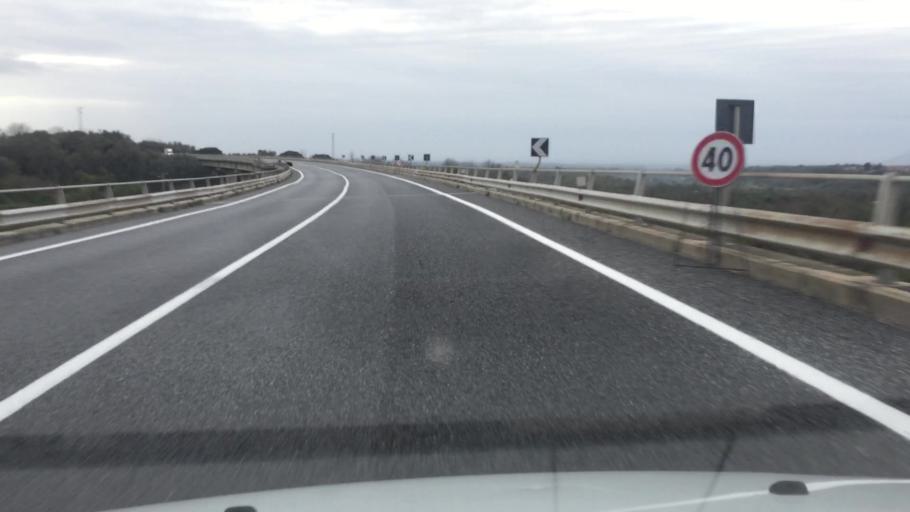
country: IT
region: Calabria
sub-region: Provincia di Reggio Calabria
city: Anoia Superiore
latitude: 38.4214
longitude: 16.0971
